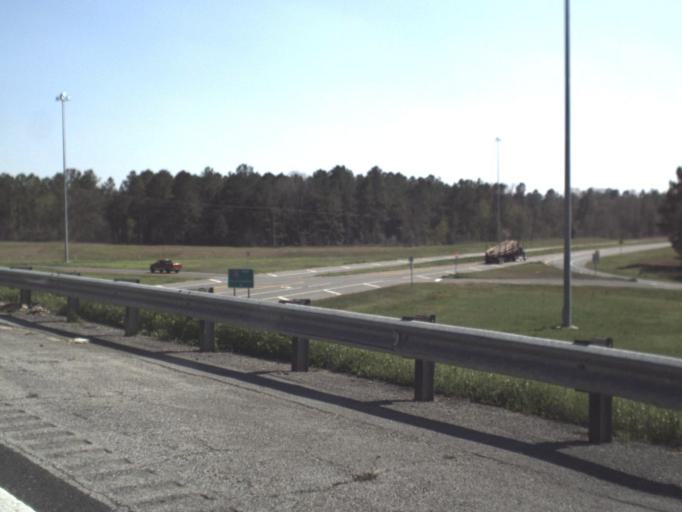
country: US
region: Florida
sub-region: Jackson County
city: Sneads
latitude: 30.6572
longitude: -85.0386
